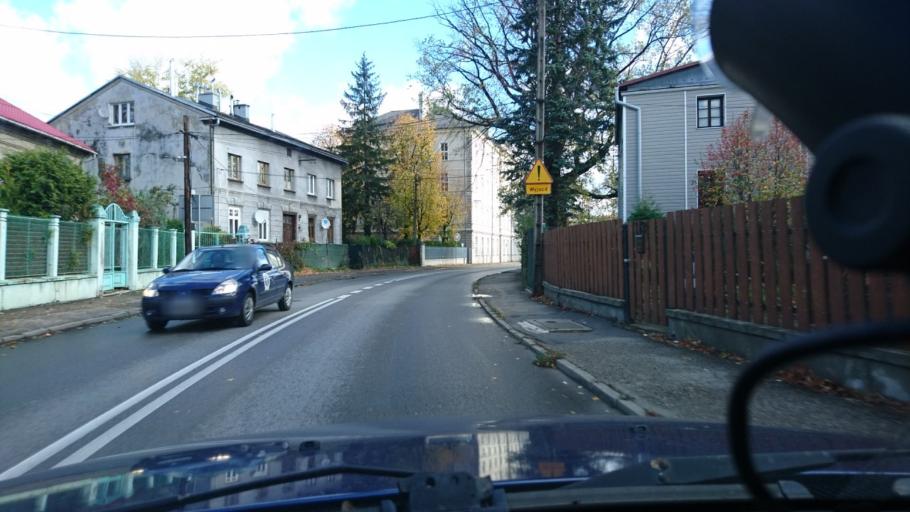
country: PL
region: Silesian Voivodeship
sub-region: Bielsko-Biala
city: Bielsko-Biala
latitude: 49.8195
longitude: 19.0274
